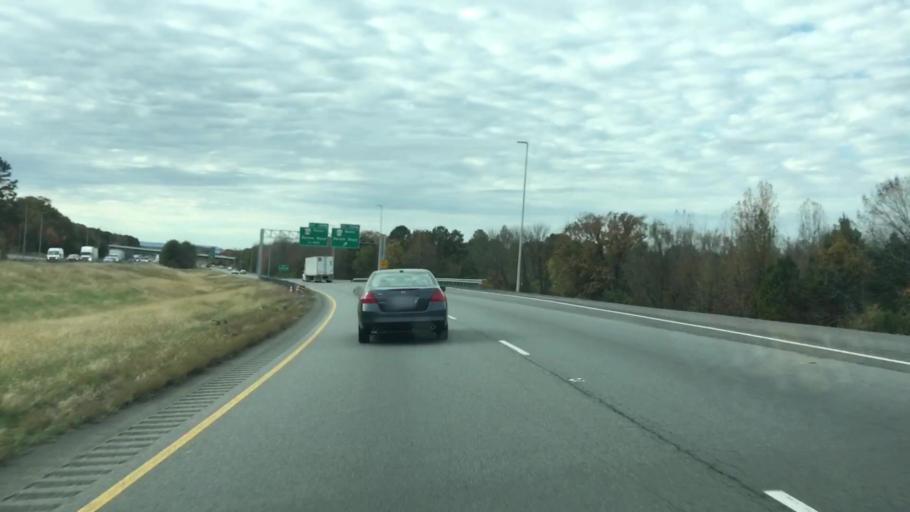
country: US
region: Arkansas
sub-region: Faulkner County
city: Conway
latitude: 35.1186
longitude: -92.4525
